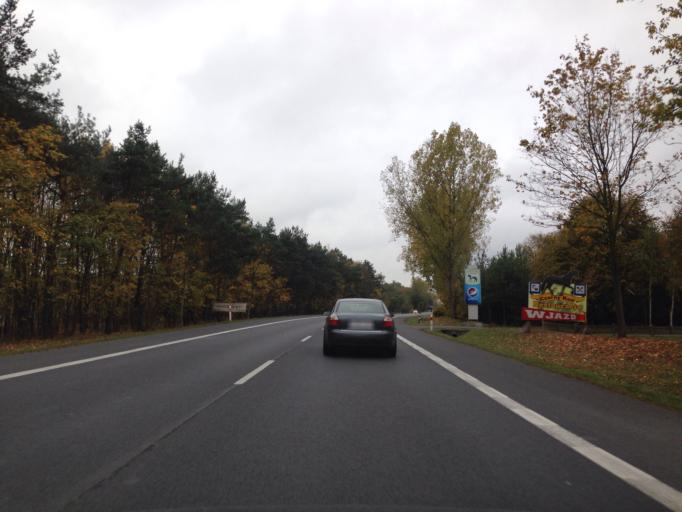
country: PL
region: Kujawsko-Pomorskie
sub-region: Powiat bydgoski
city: Osielsko
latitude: 53.2127
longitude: 18.1123
